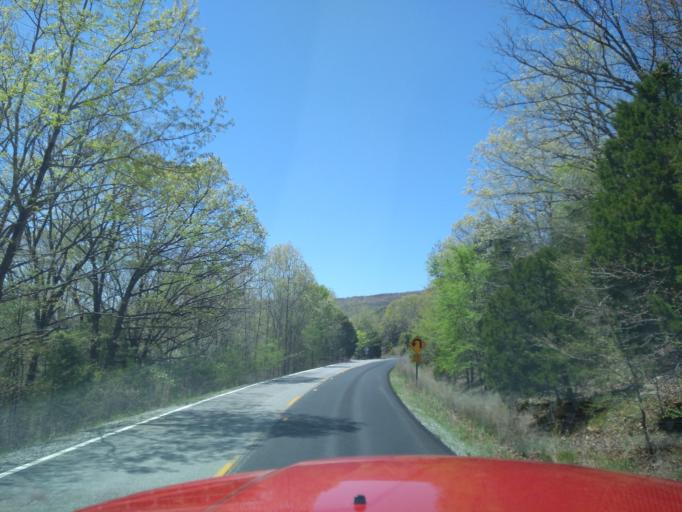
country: US
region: Arkansas
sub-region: Washington County
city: West Fork
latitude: 35.7779
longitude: -94.2626
